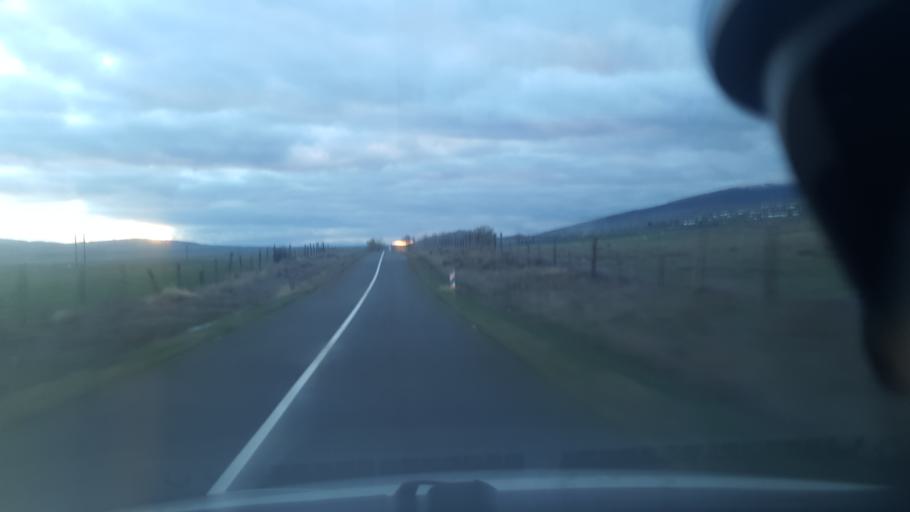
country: ES
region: Castille and Leon
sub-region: Provincia de Segovia
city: Villacastin
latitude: 40.6972
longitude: -4.3943
